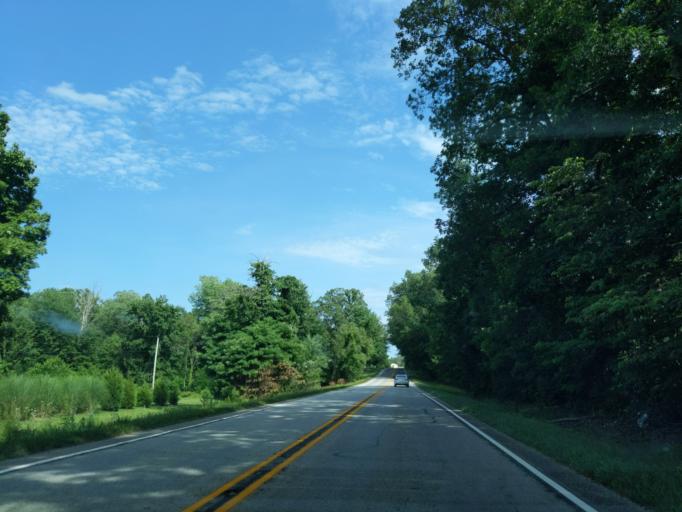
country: US
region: Indiana
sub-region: Ripley County
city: Sunman
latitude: 39.2756
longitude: -85.1096
